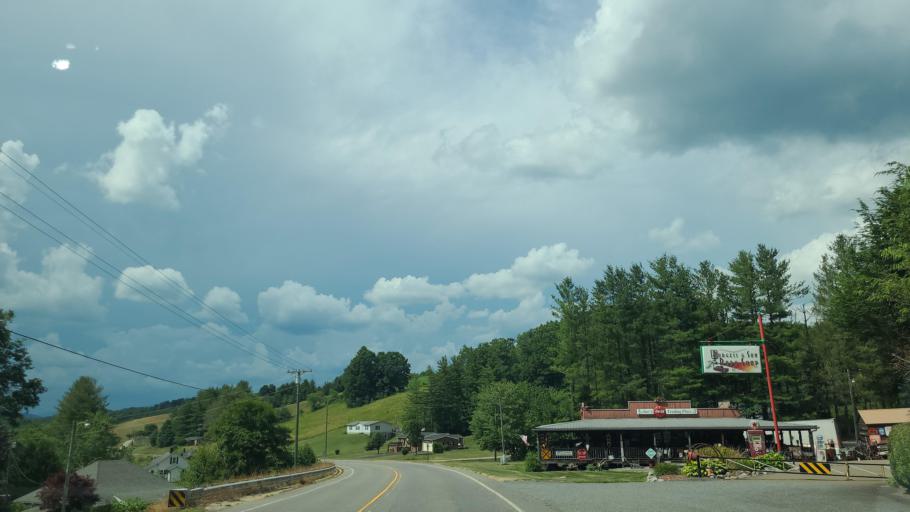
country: US
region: North Carolina
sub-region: Ashe County
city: Jefferson
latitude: 36.3565
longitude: -81.3861
